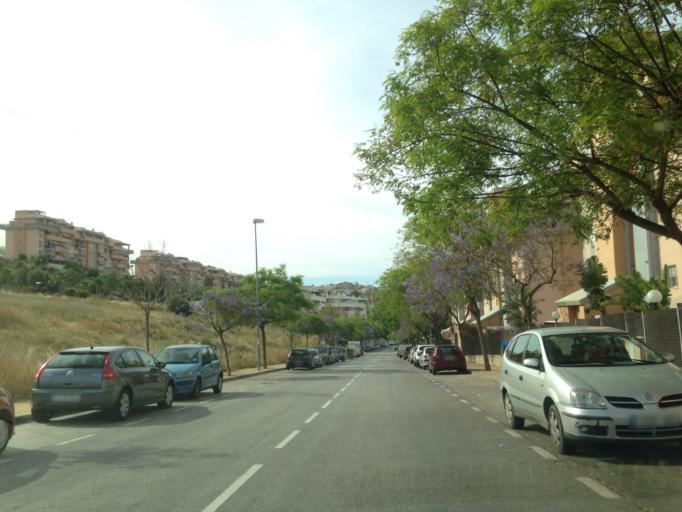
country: ES
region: Andalusia
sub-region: Provincia de Malaga
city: Malaga
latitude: 36.7549
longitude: -4.4218
